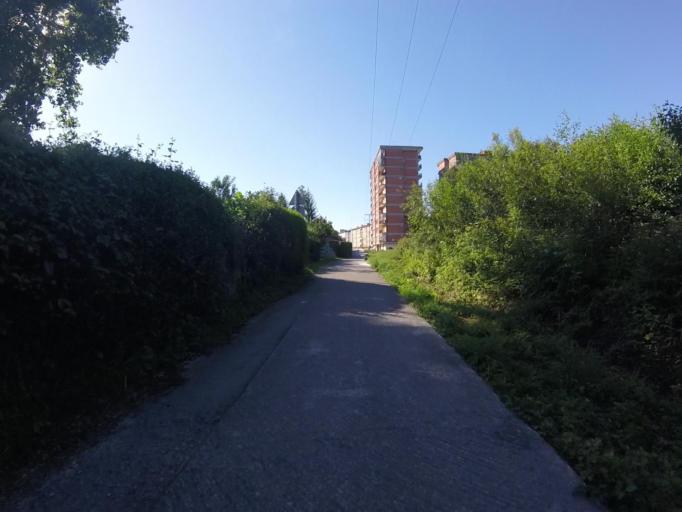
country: ES
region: Basque Country
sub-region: Provincia de Guipuzcoa
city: Irun
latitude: 43.3348
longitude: -1.7796
